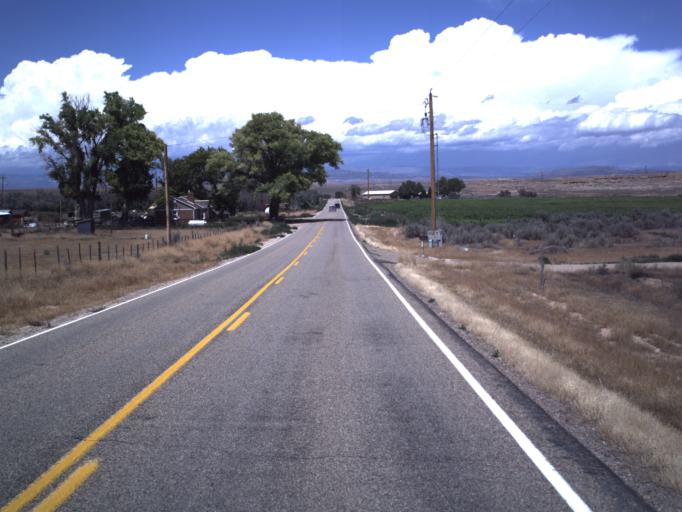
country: US
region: Utah
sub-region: Uintah County
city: Maeser
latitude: 40.2386
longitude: -109.6844
